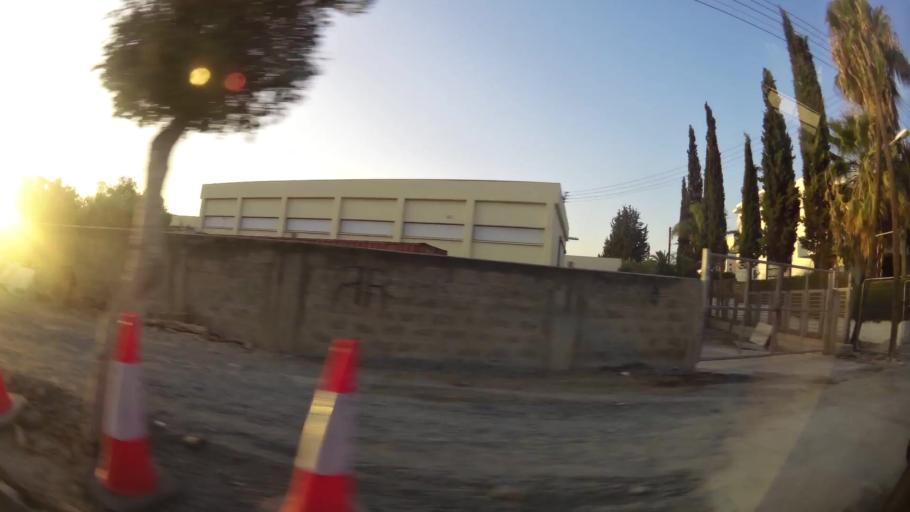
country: CY
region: Larnaka
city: Larnaca
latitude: 34.9231
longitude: 33.6091
